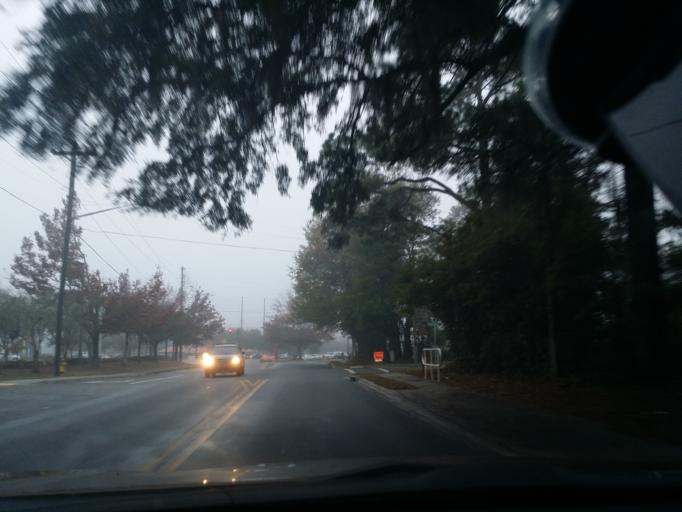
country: US
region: Florida
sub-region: Leon County
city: Tallahassee
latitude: 30.4676
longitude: -84.2835
